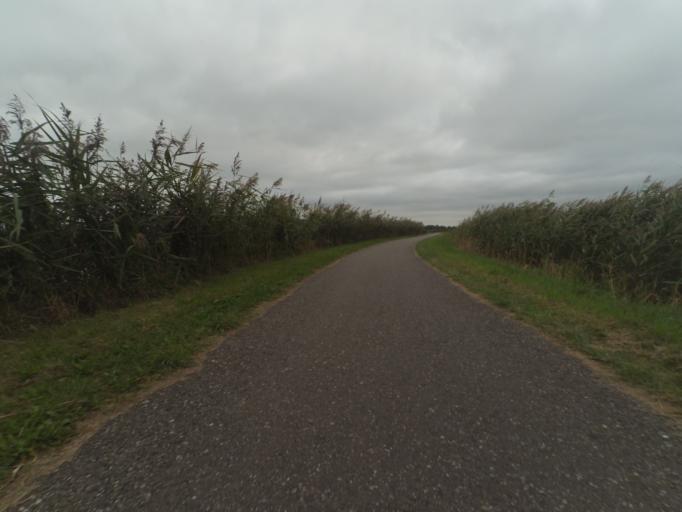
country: NL
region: Utrecht
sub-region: Gemeente Rhenen
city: Rhenen
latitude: 51.9934
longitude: 5.6100
